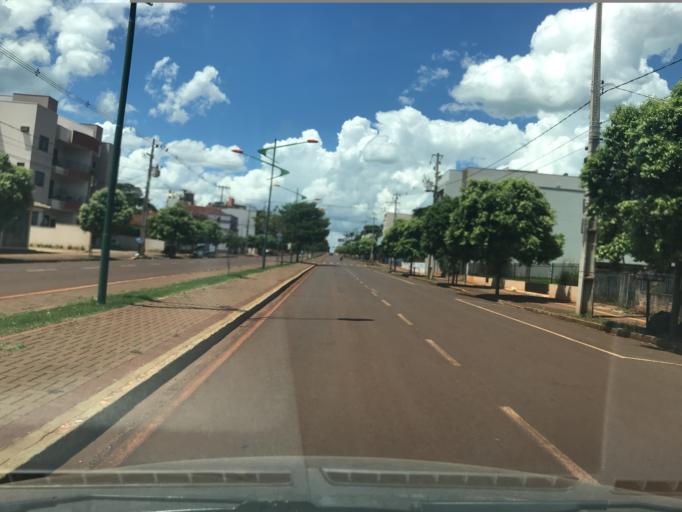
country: BR
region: Parana
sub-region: Palotina
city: Palotina
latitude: -24.2847
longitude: -53.8457
